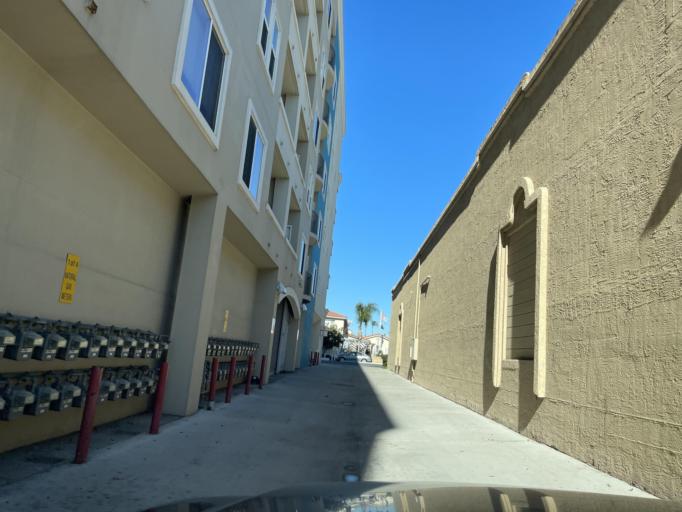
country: US
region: California
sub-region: San Diego County
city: National City
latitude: 32.6767
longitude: -117.1021
